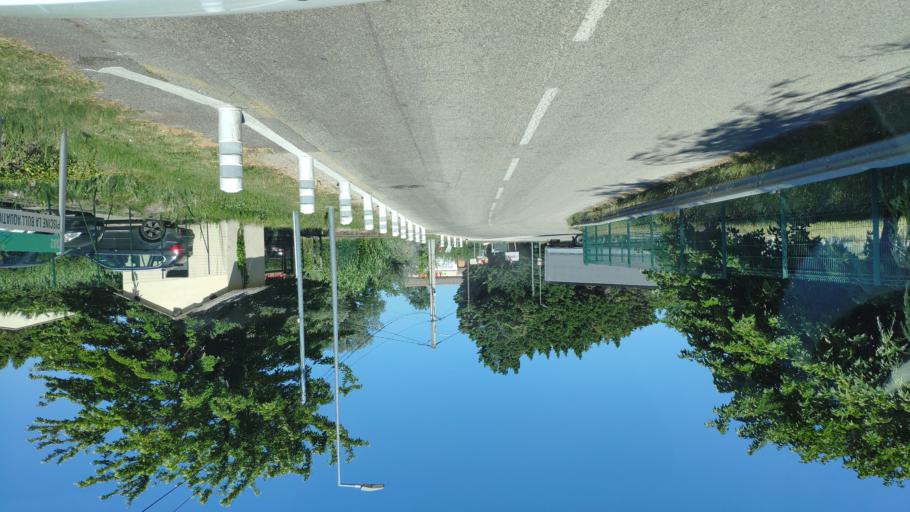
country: FR
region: Provence-Alpes-Cote d'Azur
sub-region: Departement du Vaucluse
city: Chateauneuf-de-Gadagne
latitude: 43.9302
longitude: 4.9524
